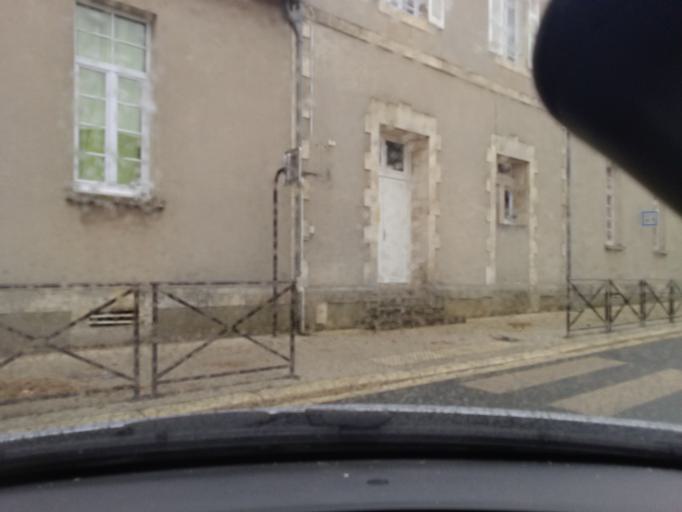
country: FR
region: Pays de la Loire
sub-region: Departement de la Vendee
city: Sainte-Gemme-la-Plaine
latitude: 46.4808
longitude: -1.1121
